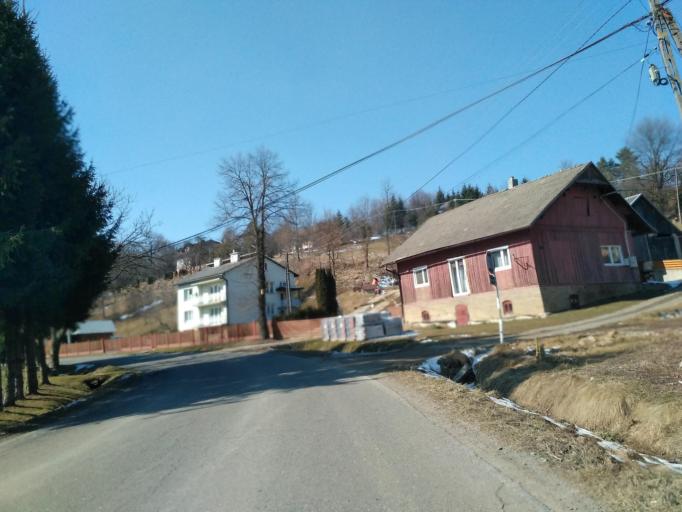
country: PL
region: Subcarpathian Voivodeship
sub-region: Powiat brzozowski
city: Jasienica Rosielna
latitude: 49.7553
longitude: 21.9062
